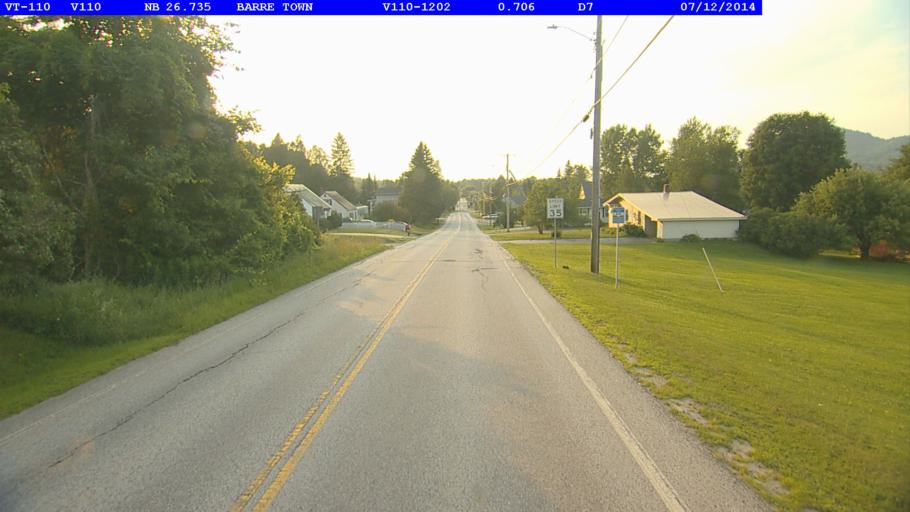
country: US
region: Vermont
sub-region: Washington County
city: South Barre
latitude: 44.1562
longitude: -72.4479
